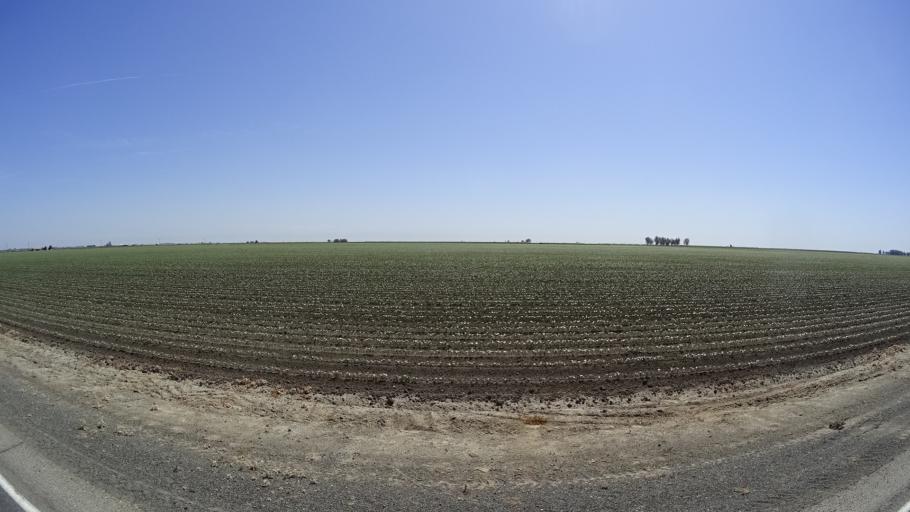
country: US
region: California
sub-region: Kings County
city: Stratford
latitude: 36.1918
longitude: -119.7803
